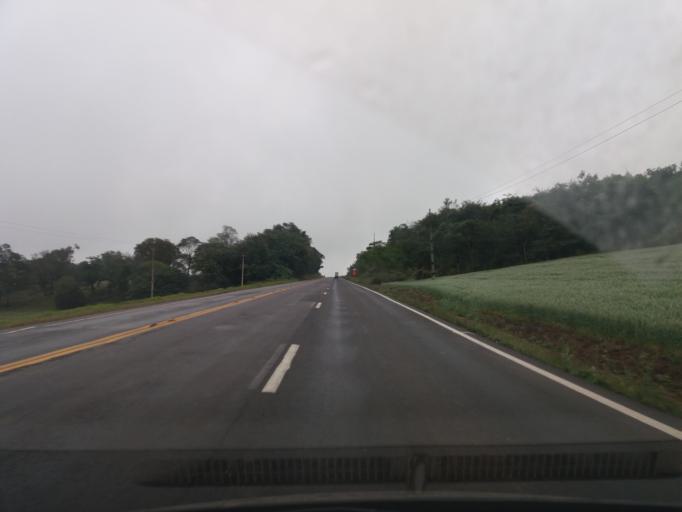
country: BR
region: Parana
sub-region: Realeza
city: Realeza
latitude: -25.5590
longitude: -53.5829
